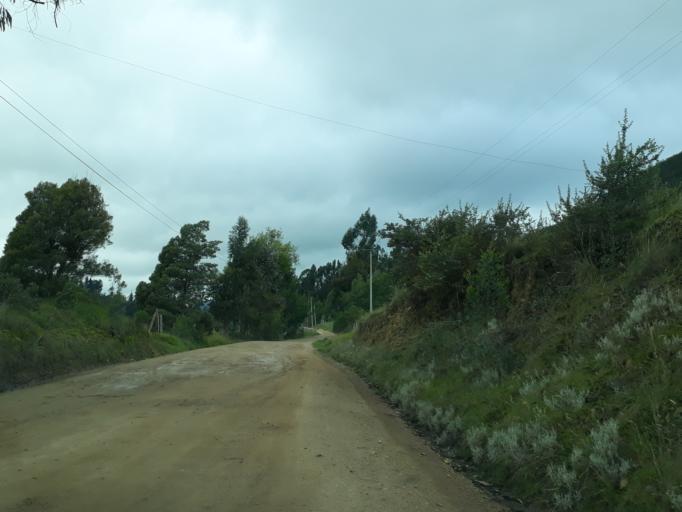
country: CO
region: Cundinamarca
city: Cucunuba
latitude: 5.2002
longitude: -73.7762
